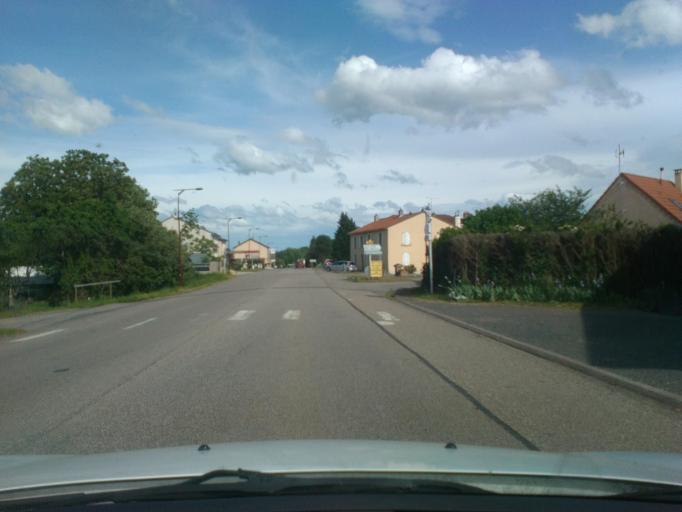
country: FR
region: Lorraine
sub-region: Departement de Meurthe-et-Moselle
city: Baccarat
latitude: 48.5500
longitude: 6.7228
